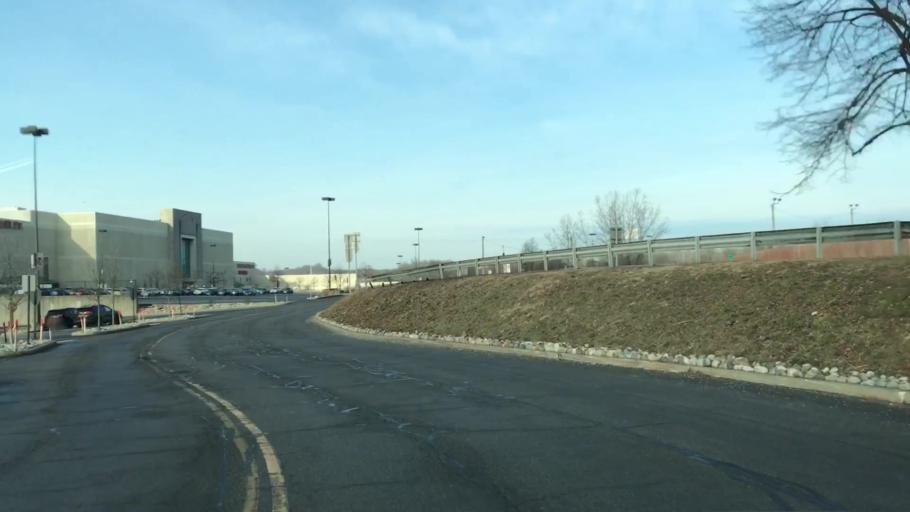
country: US
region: New York
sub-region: Rockland County
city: Valley Cottage
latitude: 41.0982
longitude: -73.9523
